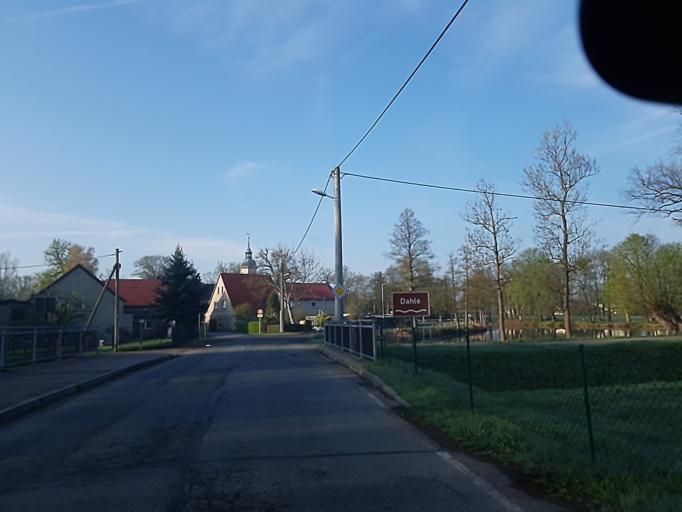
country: DE
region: Saxony
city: Cavertitz
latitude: 51.3622
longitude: 13.0832
